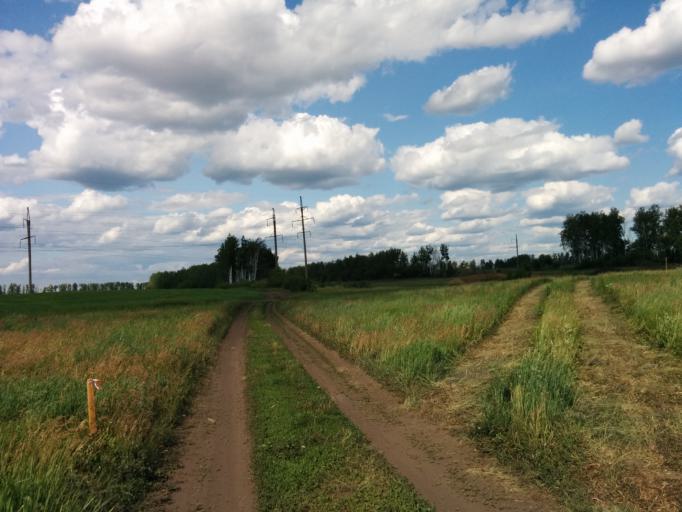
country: RU
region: Tambov
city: Tambov
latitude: 52.7960
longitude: 41.3815
